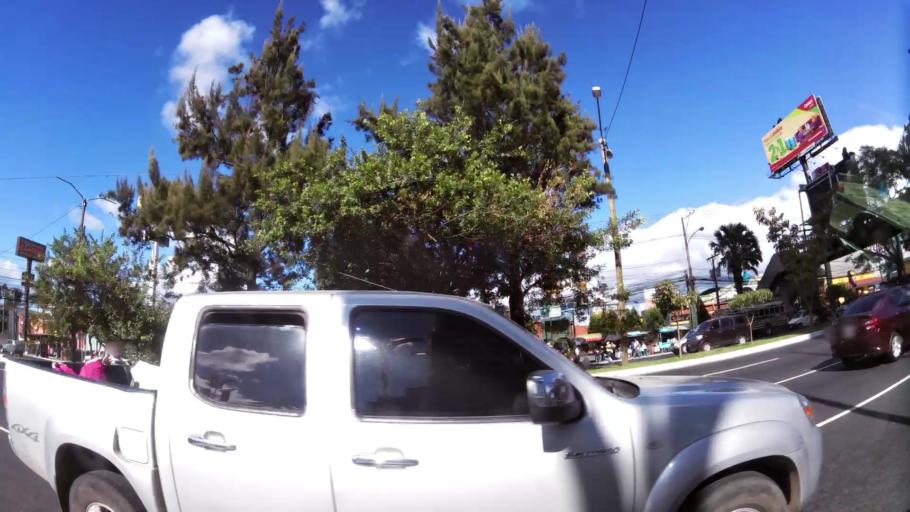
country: GT
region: Guatemala
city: Guatemala City
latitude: 14.6238
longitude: -90.5534
